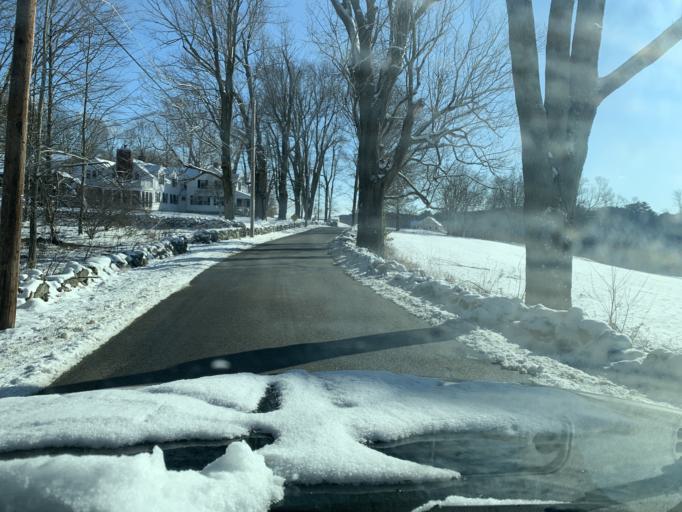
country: US
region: Massachusetts
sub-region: Essex County
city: Topsfield
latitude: 42.6316
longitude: -70.9549
